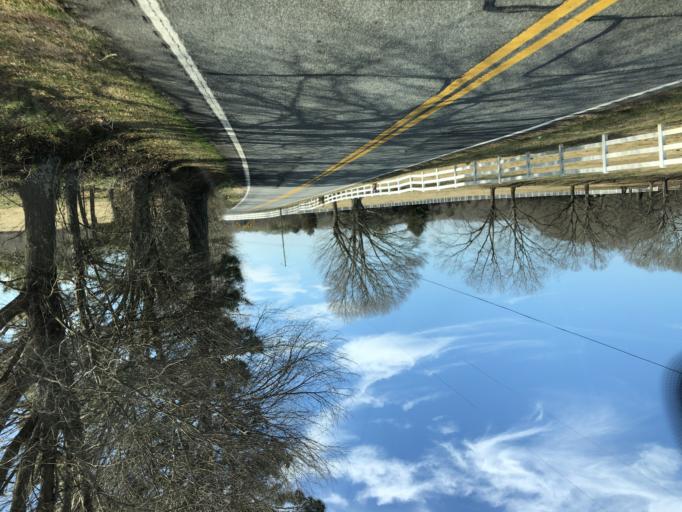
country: US
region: South Carolina
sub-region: Spartanburg County
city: Mayo
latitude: 35.0536
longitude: -81.9051
